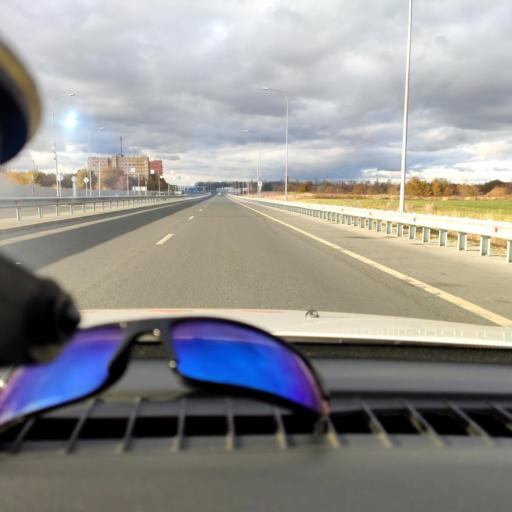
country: RU
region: Samara
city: Bereza
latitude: 53.5149
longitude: 50.1515
